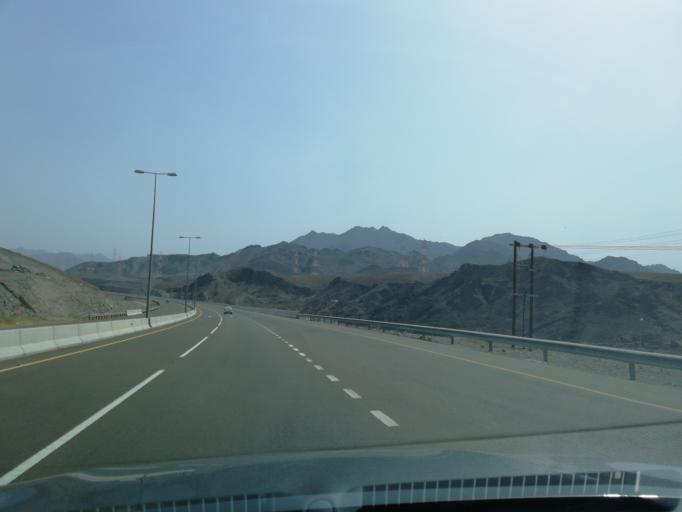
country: OM
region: Al Batinah
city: Al Liwa'
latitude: 24.2576
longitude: 56.3590
